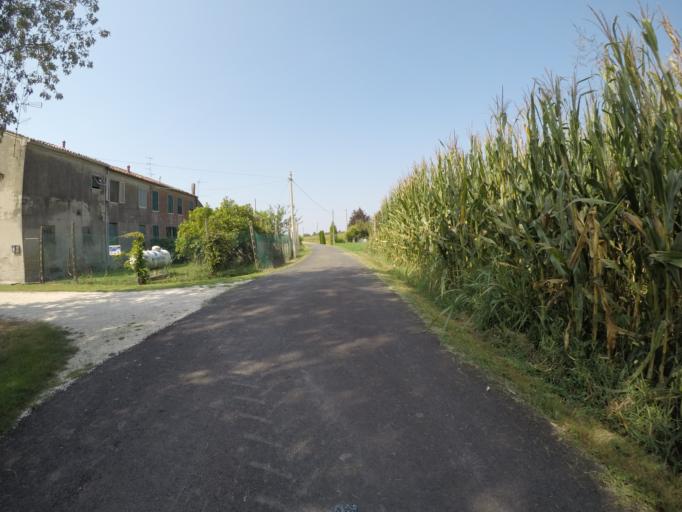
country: IT
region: Veneto
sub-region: Provincia di Rovigo
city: Lendinara
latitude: 45.1092
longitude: 11.6045
